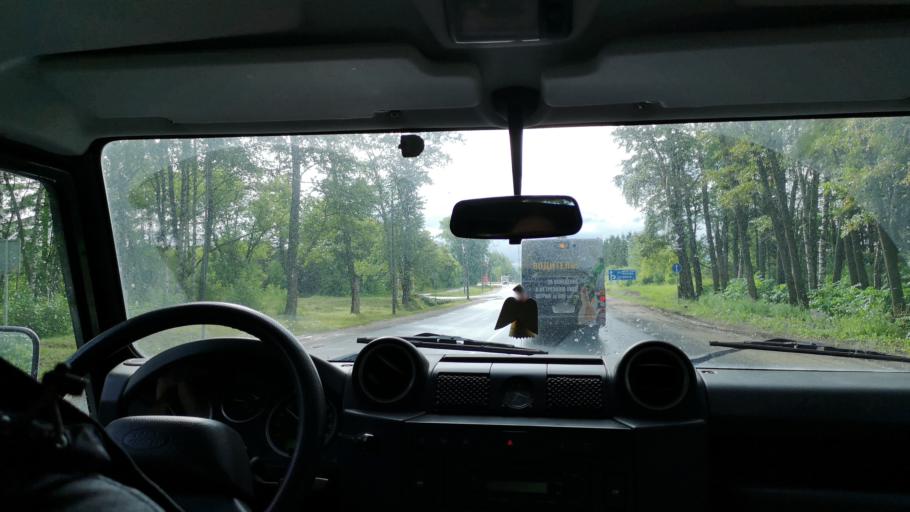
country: RU
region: Moskovskaya
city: Gorshkovo
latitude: 56.3667
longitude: 37.4646
